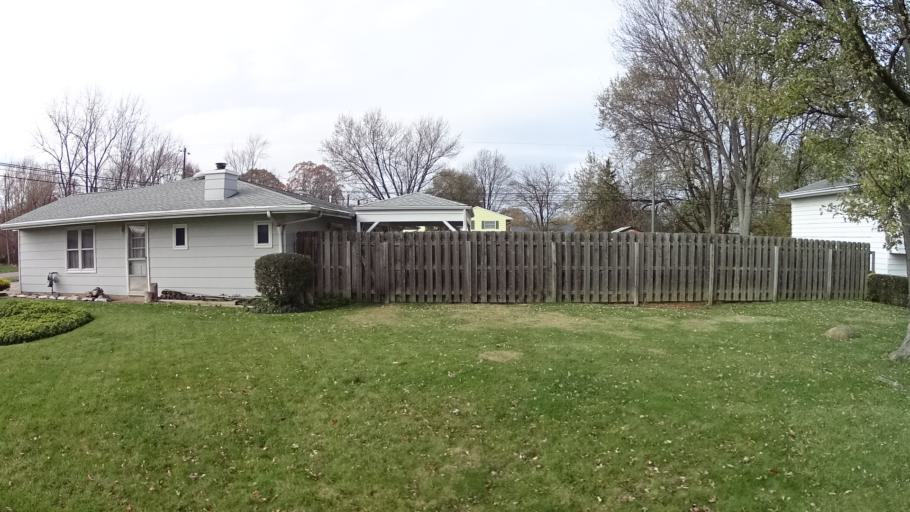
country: US
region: Ohio
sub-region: Lorain County
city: Sheffield Lake
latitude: 41.4829
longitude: -82.1143
